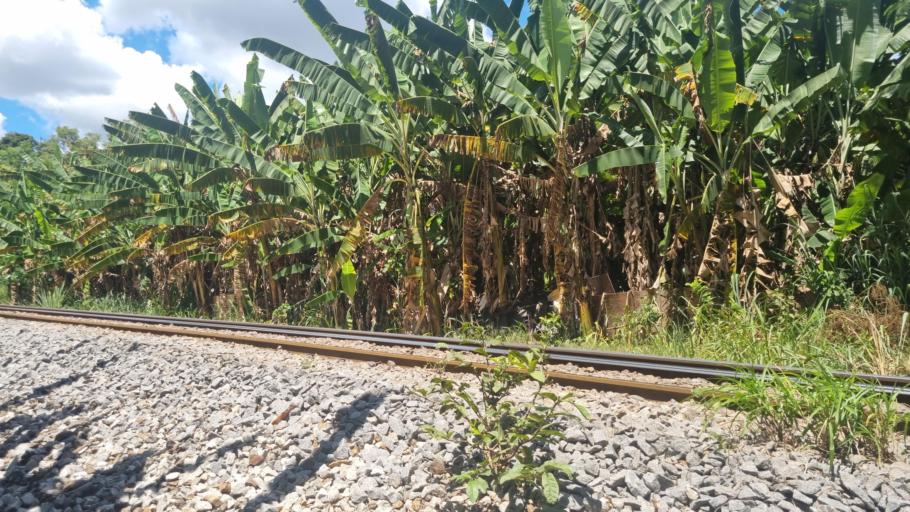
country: BR
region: Minas Gerais
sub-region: Santa Luzia
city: Santa Luzia
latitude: -19.8344
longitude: -43.8671
